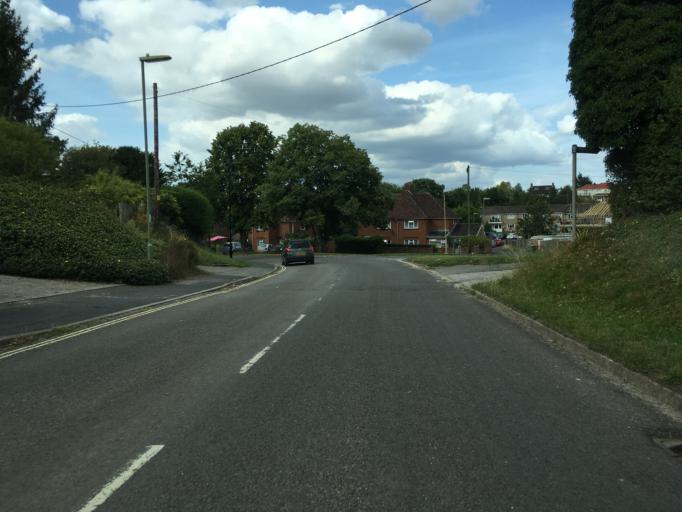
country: GB
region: England
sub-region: Hampshire
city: Overton
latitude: 51.2397
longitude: -1.2621
